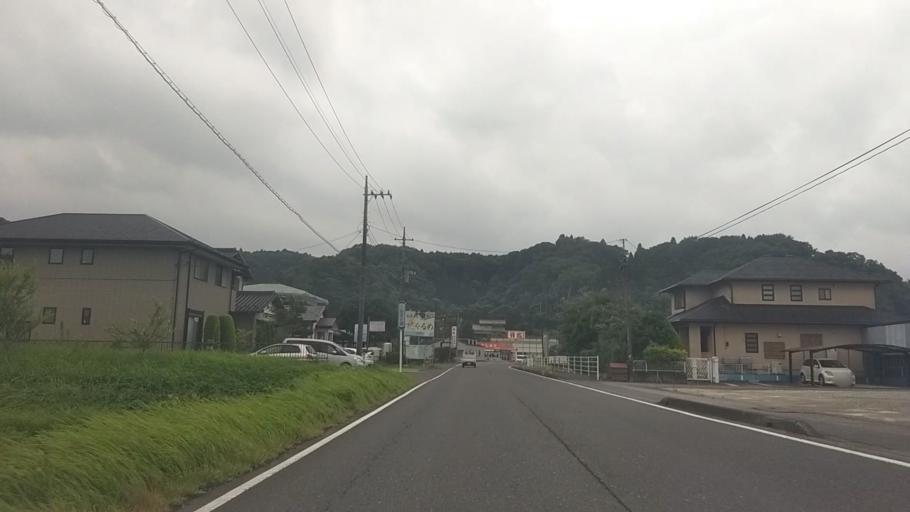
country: JP
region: Chiba
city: Kisarazu
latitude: 35.2876
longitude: 140.0832
